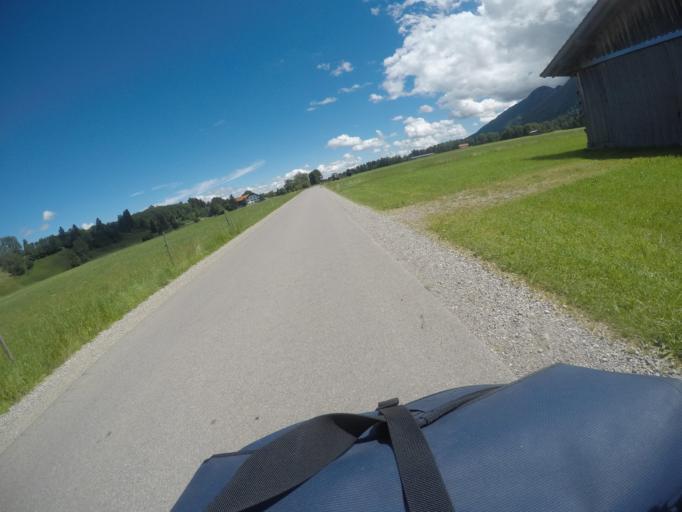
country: DE
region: Bavaria
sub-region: Swabia
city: Halblech
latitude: 47.6266
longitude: 10.8072
